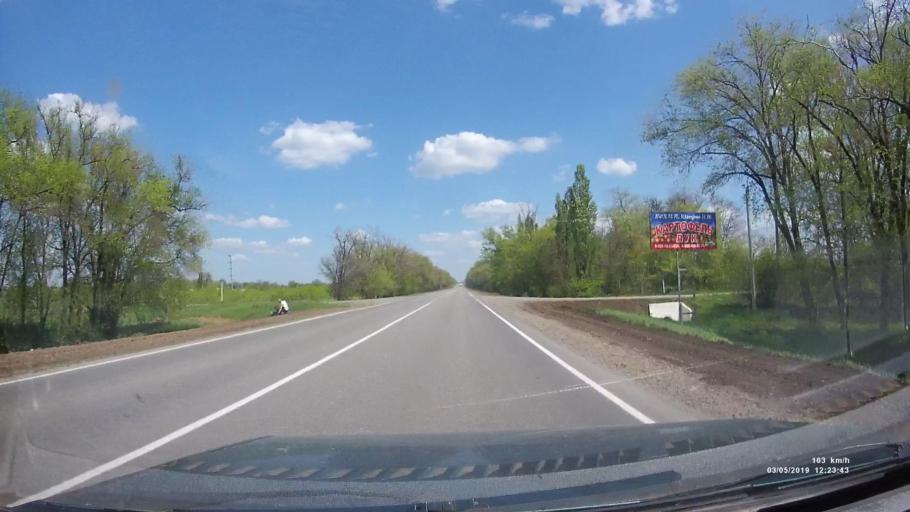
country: RU
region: Rostov
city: Semikarakorsk
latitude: 47.4121
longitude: 40.6878
